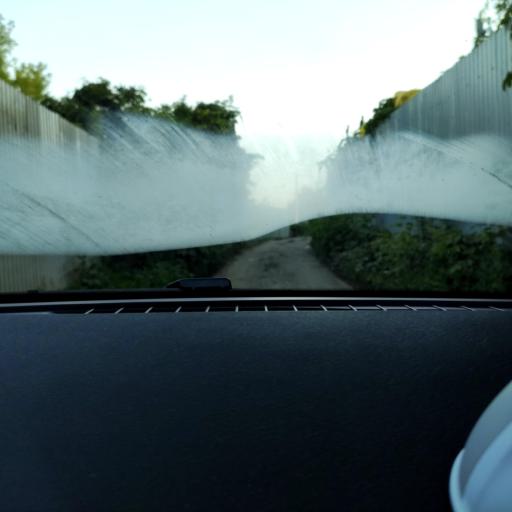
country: RU
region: Samara
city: Petra-Dubrava
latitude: 53.2591
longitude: 50.3065
